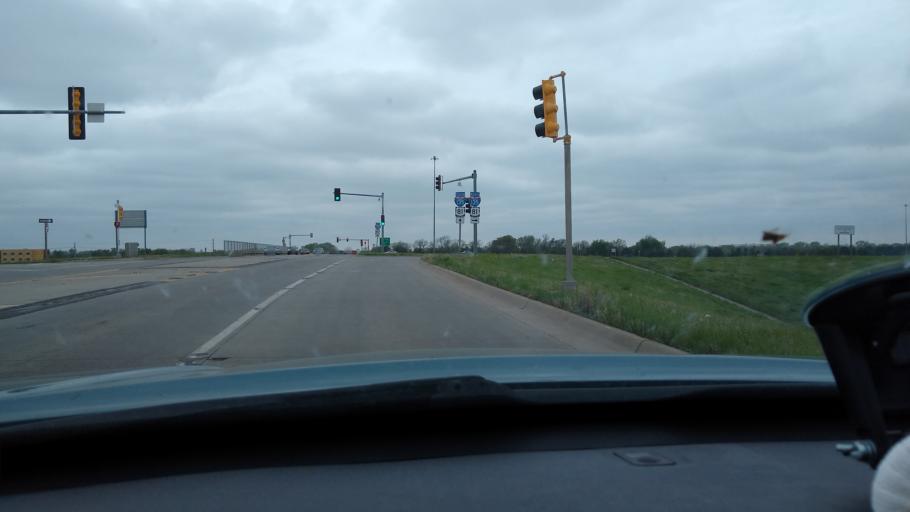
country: US
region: Kansas
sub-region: Saline County
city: Salina
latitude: 38.7982
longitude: -97.6168
